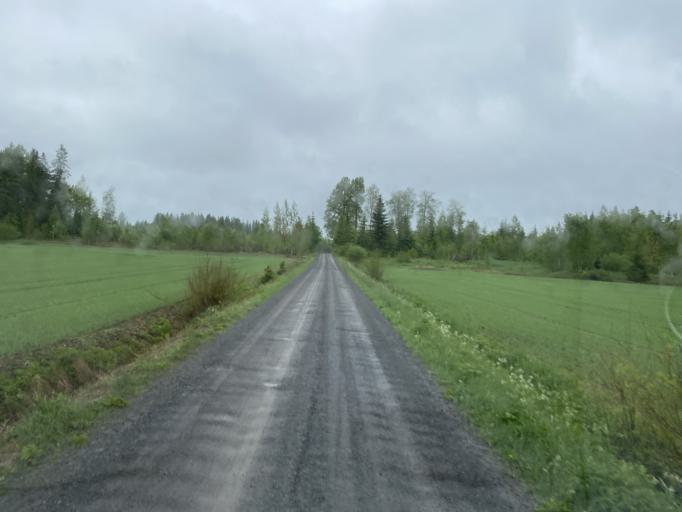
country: FI
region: Haeme
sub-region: Forssa
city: Forssa
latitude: 60.9538
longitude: 23.5994
